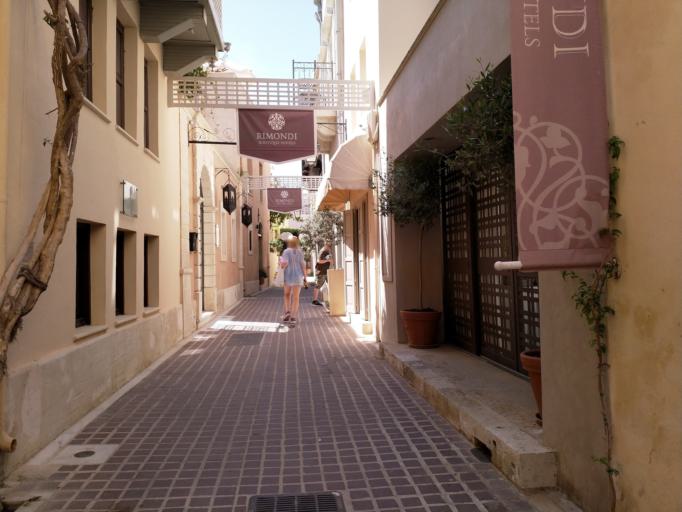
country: GR
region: Crete
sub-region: Nomos Rethymnis
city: Rethymno
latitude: 35.3699
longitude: 24.4740
